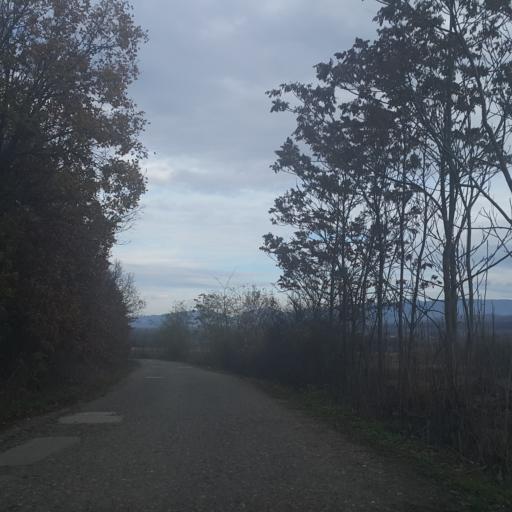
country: RS
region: Central Serbia
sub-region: Zajecarski Okrug
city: Knjazevac
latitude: 43.6088
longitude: 22.2590
